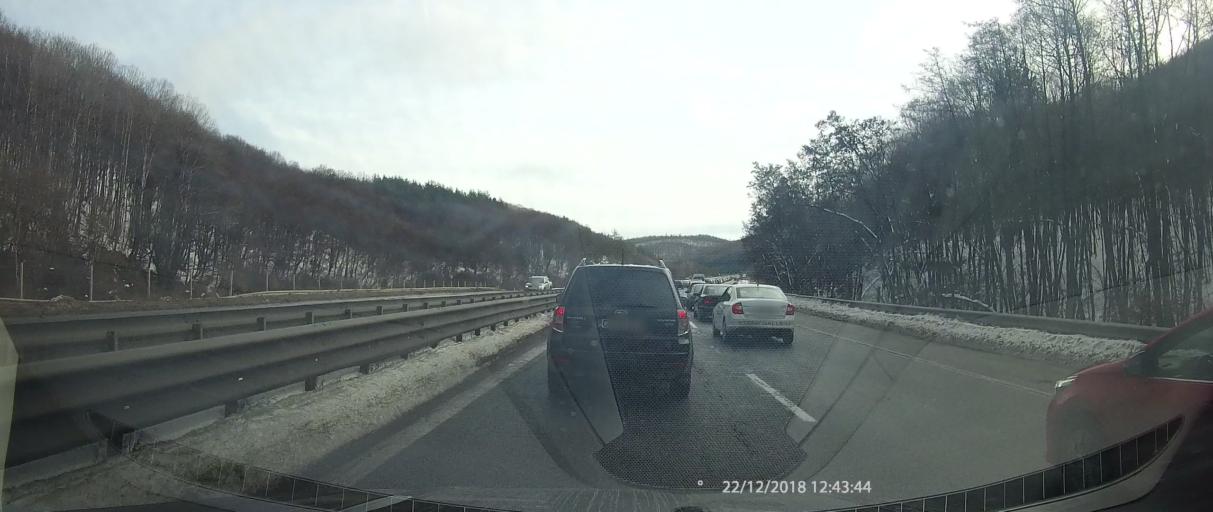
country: BG
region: Sofiya
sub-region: Obshtina Gorna Malina
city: Gorna Malina
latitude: 42.7794
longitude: 23.7693
